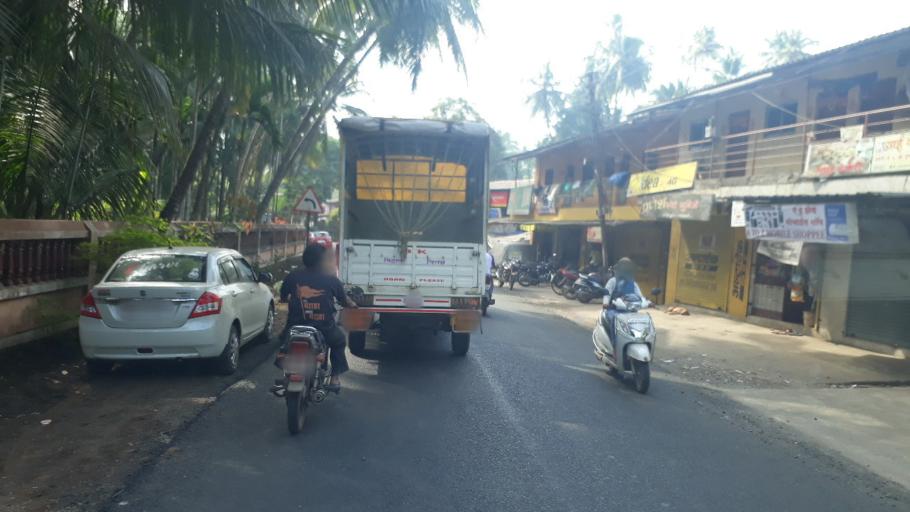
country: IN
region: Maharashtra
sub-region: Raigarh
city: Revadanda
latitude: 18.5812
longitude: 72.9244
